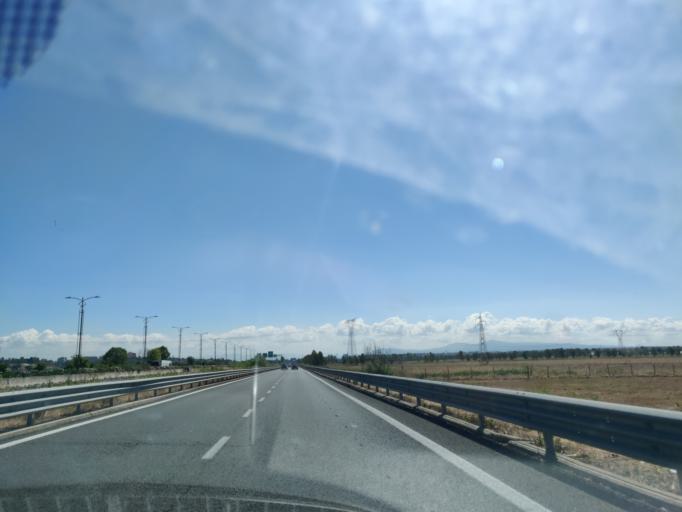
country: IT
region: Latium
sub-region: Citta metropolitana di Roma Capitale
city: Ponte Galeria-La Pisana
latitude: 41.8156
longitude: 12.3640
